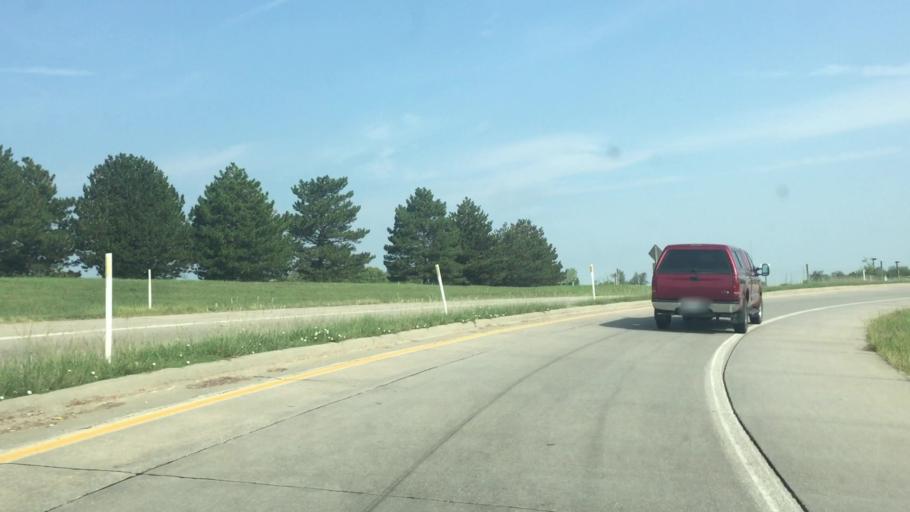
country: US
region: Kansas
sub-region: Butler County
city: Andover
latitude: 37.6892
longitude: -97.1877
